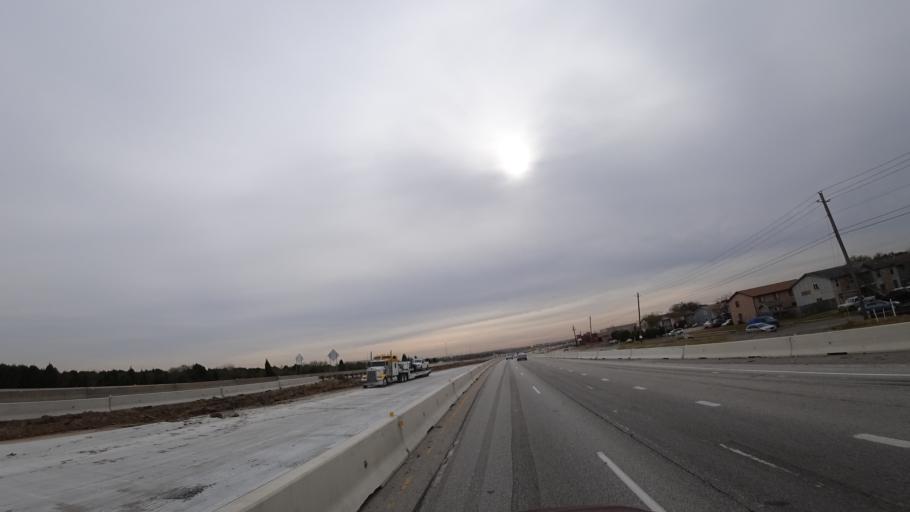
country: US
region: Texas
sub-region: Travis County
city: Austin
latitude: 30.3201
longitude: -97.6663
